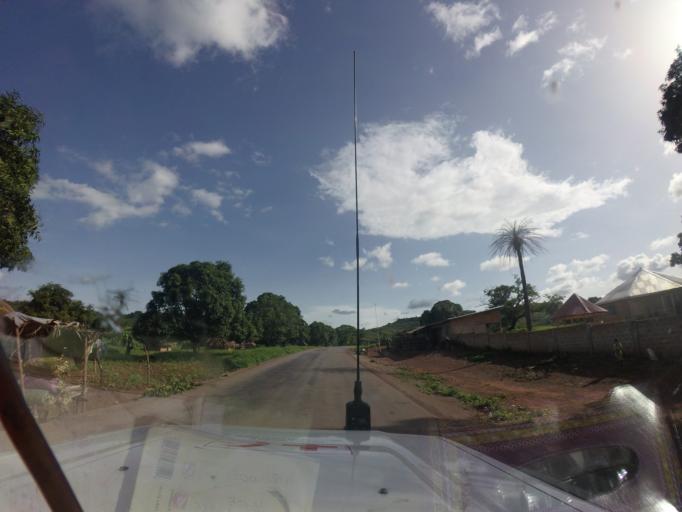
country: GN
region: Mamou
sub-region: Mamou Prefecture
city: Mamou
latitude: 10.1819
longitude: -12.4611
